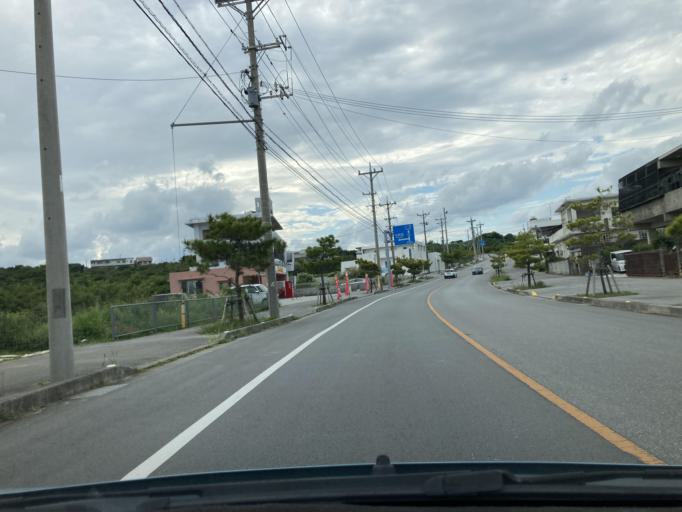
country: JP
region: Okinawa
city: Katsuren-haebaru
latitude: 26.3270
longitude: 127.8976
